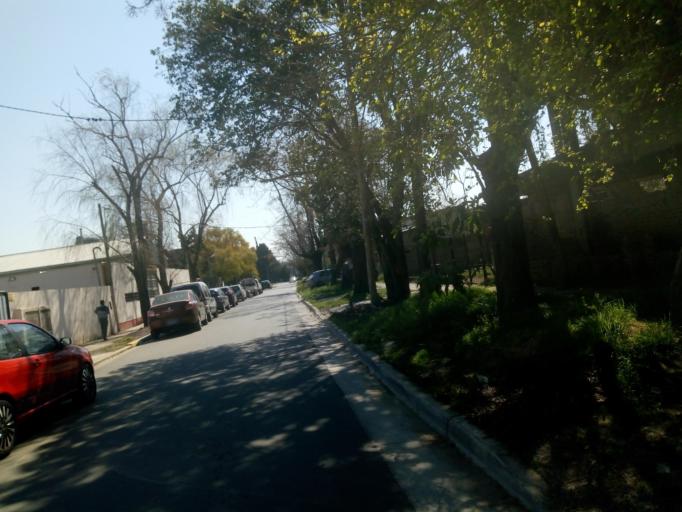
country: AR
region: Buenos Aires
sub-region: Partido de La Plata
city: La Plata
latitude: -34.9100
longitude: -57.9252
